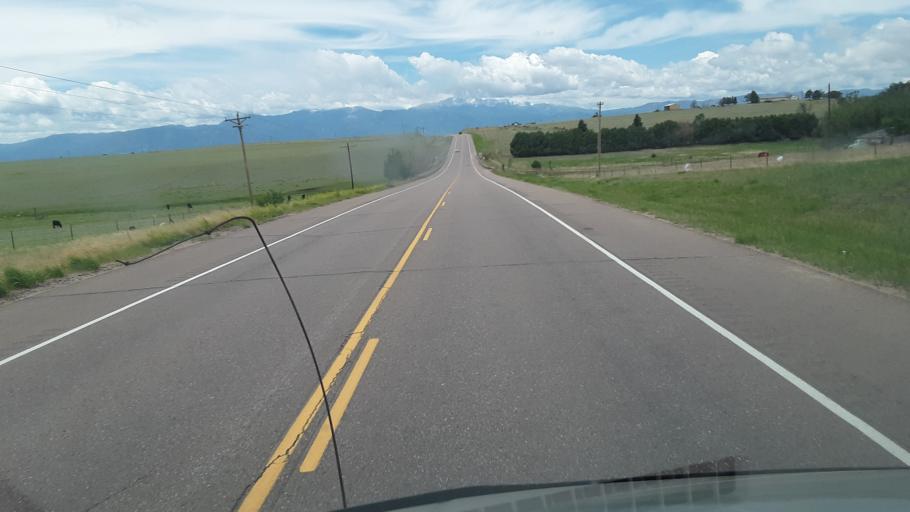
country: US
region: Colorado
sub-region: El Paso County
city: Cimarron Hills
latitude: 38.8387
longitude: -104.5626
